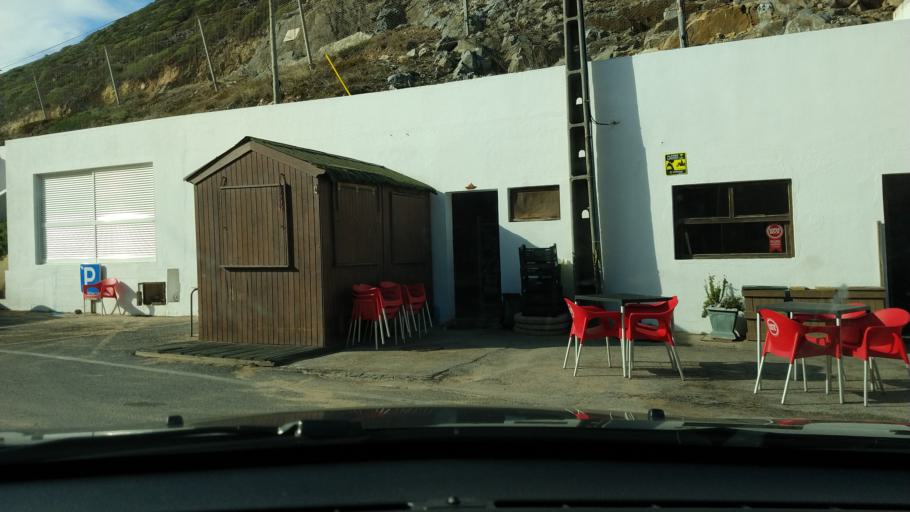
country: PT
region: Lisbon
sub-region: Sintra
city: Colares
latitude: 38.8023
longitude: -9.4847
